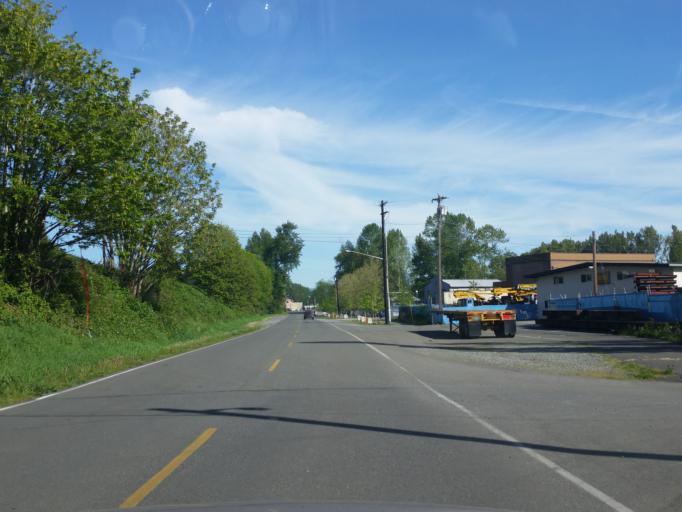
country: US
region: Washington
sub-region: Snohomish County
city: Snohomish
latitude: 47.9135
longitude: -122.1053
